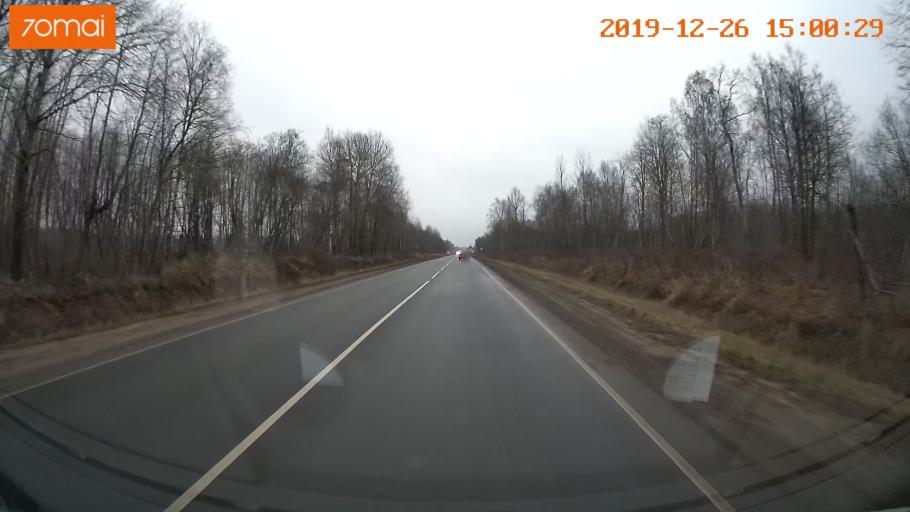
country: RU
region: Jaroslavl
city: Rybinsk
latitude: 58.2458
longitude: 38.8524
